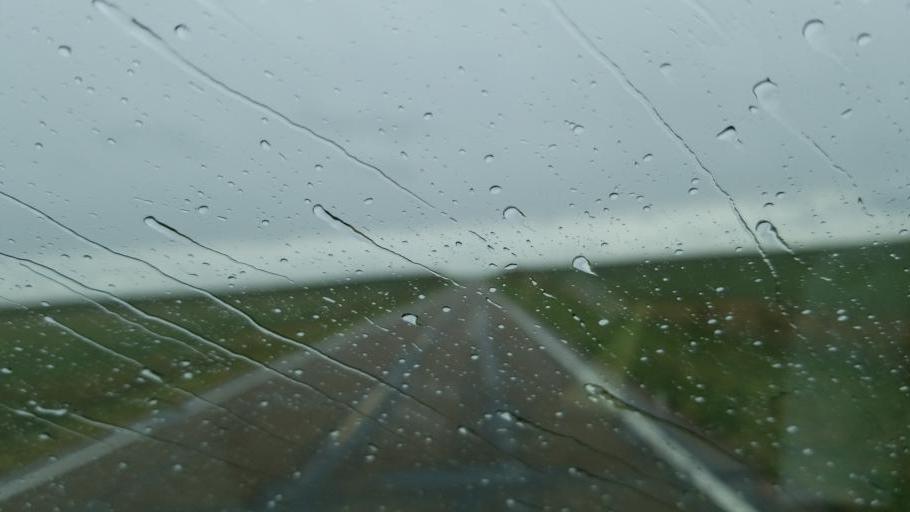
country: US
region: Colorado
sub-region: Lincoln County
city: Hugo
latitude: 38.8498
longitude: -103.1985
